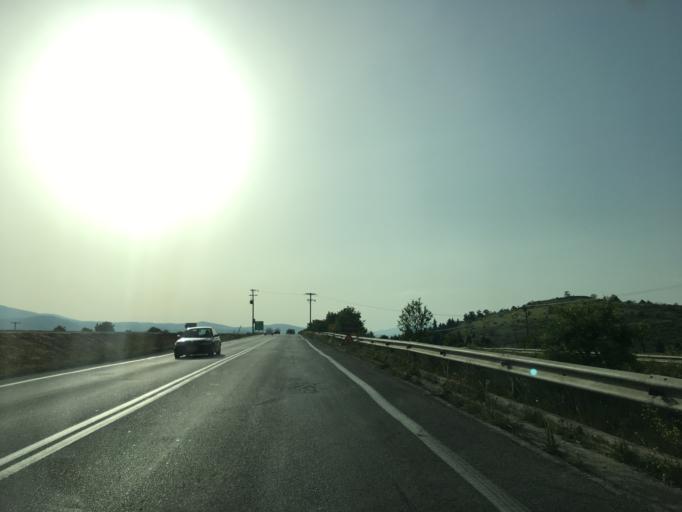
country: GR
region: Thessaly
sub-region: Nomos Magnisias
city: Velestino
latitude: 39.3861
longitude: 22.7928
